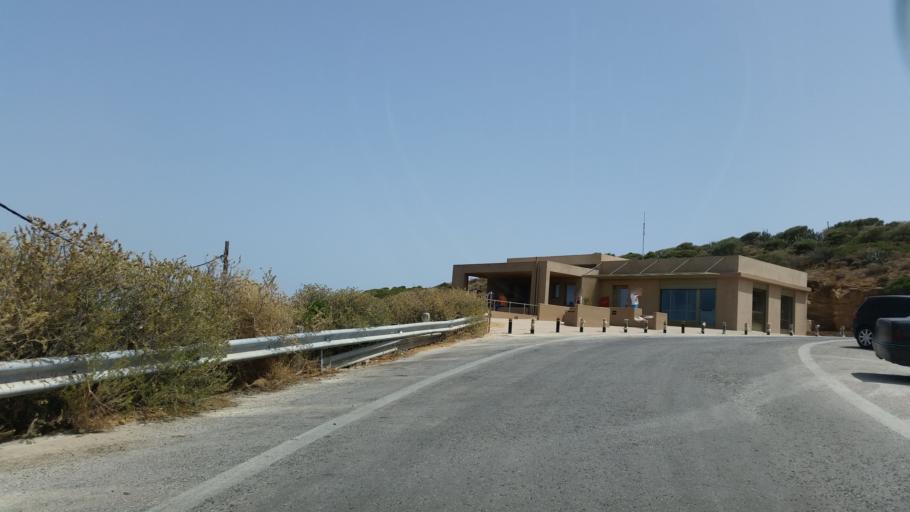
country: GR
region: Attica
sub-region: Nomarchia Anatolikis Attikis
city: Lavrio
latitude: 37.6507
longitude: 24.0272
